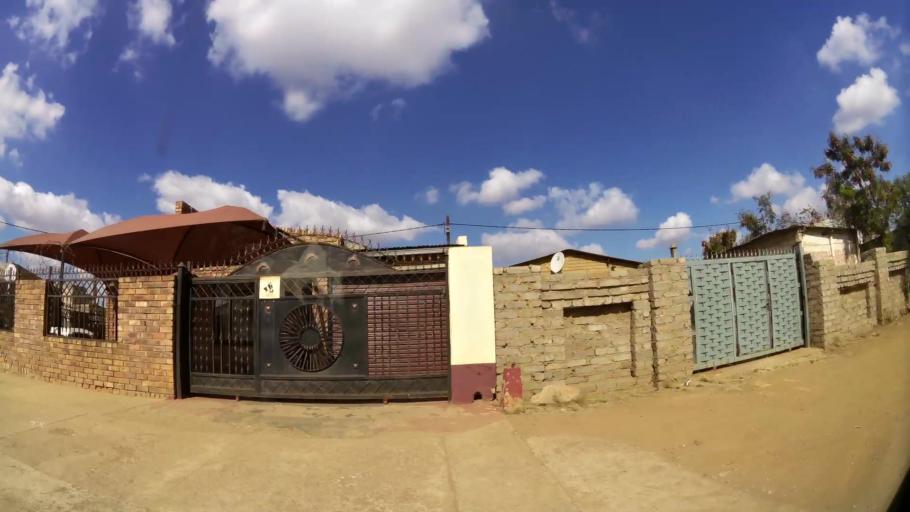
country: ZA
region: Gauteng
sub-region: City of Tshwane Metropolitan Municipality
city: Cullinan
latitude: -25.7057
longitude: 28.4089
